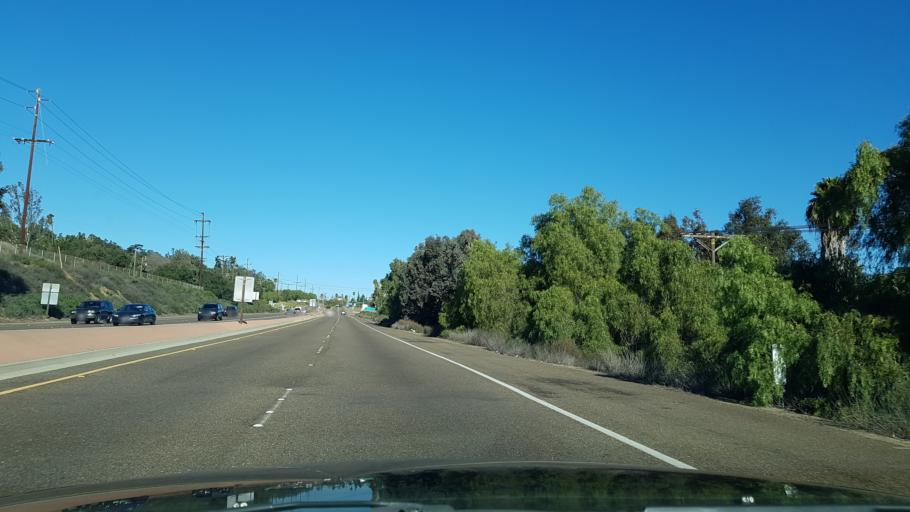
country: US
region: California
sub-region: San Diego County
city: Escondido
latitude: 33.0837
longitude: -117.0711
